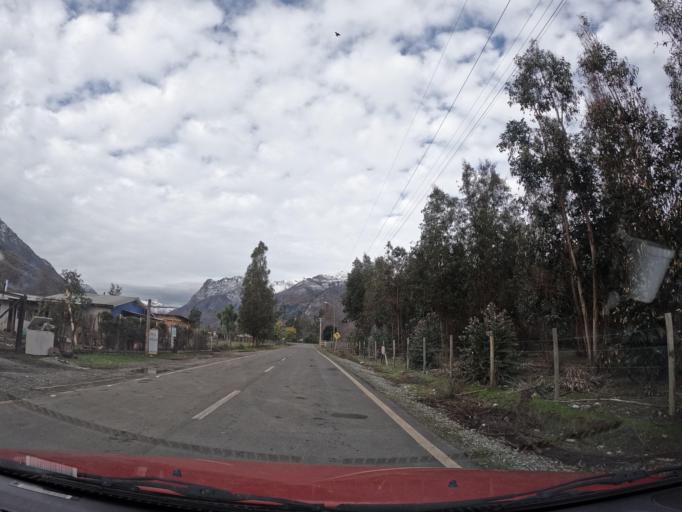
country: CL
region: Maule
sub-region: Provincia de Linares
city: Colbun
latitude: -35.8608
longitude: -71.2595
